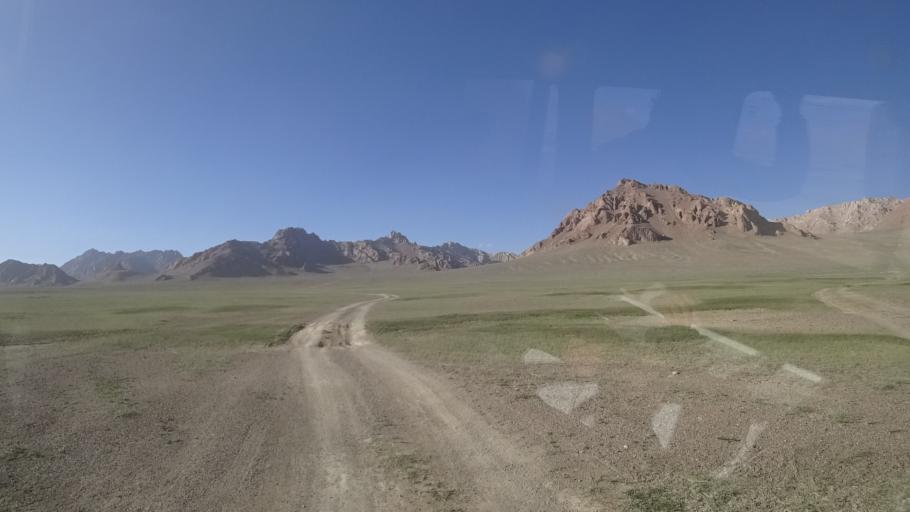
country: TJ
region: Gorno-Badakhshan
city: Murghob
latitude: 37.6628
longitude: 74.1707
